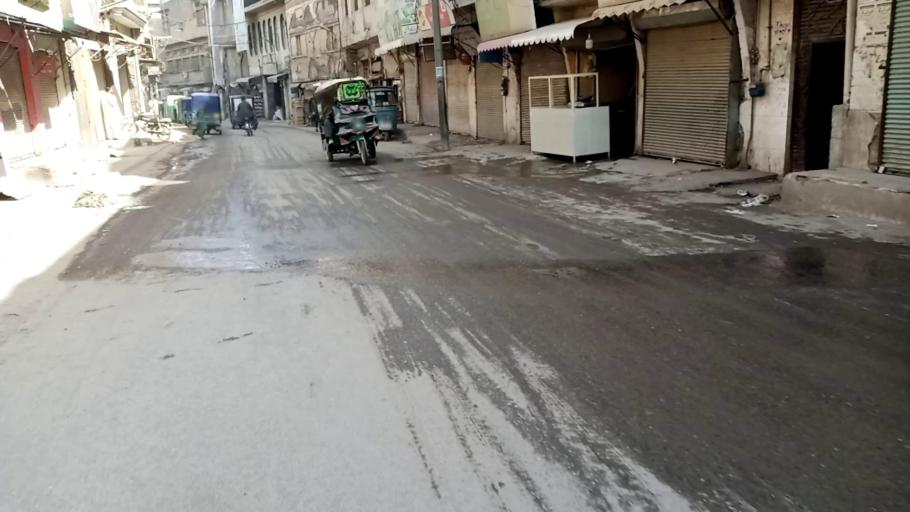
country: PK
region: Khyber Pakhtunkhwa
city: Peshawar
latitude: 33.9980
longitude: 71.5785
